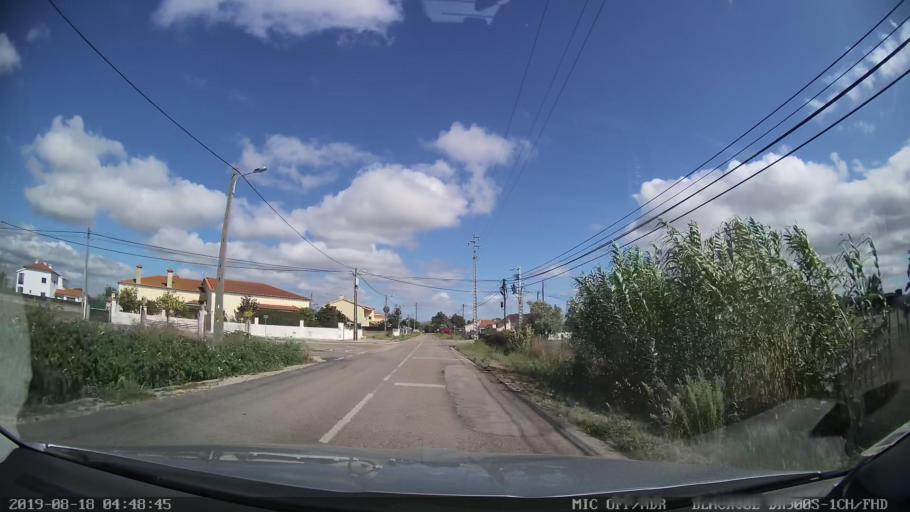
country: PT
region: Santarem
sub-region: Benavente
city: Benavente
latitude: 38.9421
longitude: -8.8024
